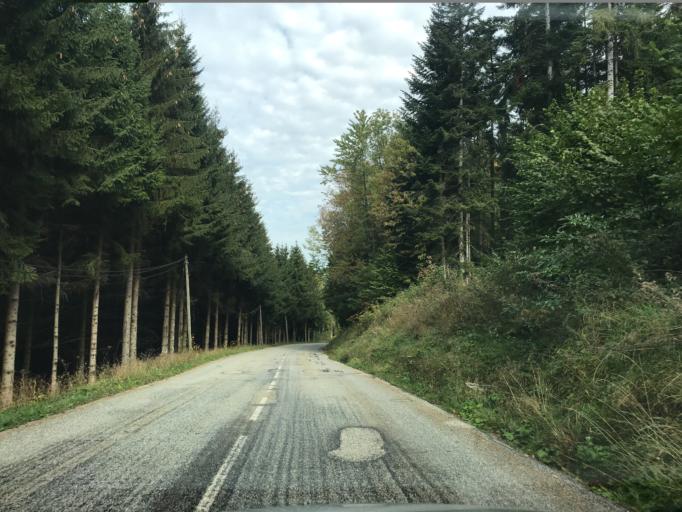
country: FR
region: Rhone-Alpes
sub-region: Departement de la Savoie
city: Les Echelles
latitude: 45.4626
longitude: 5.8263
